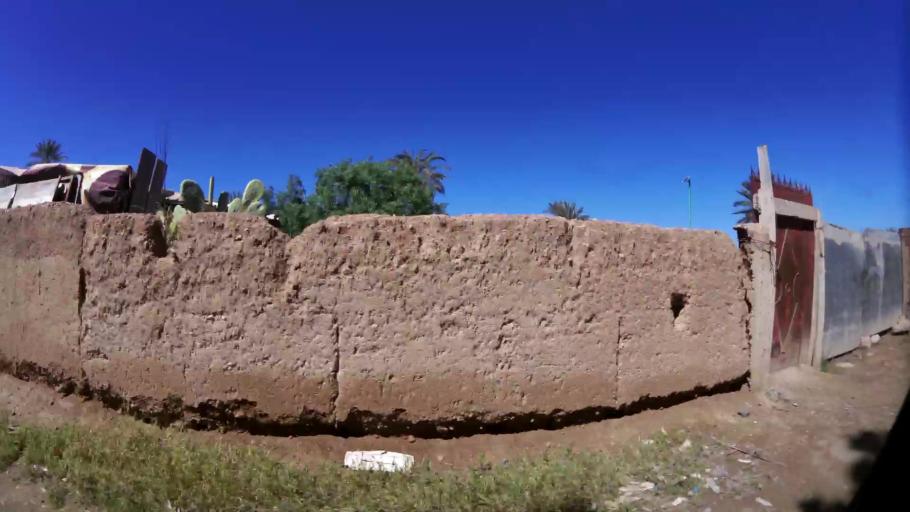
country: MA
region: Marrakech-Tensift-Al Haouz
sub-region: Marrakech
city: Marrakesh
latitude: 31.6683
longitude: -7.9595
